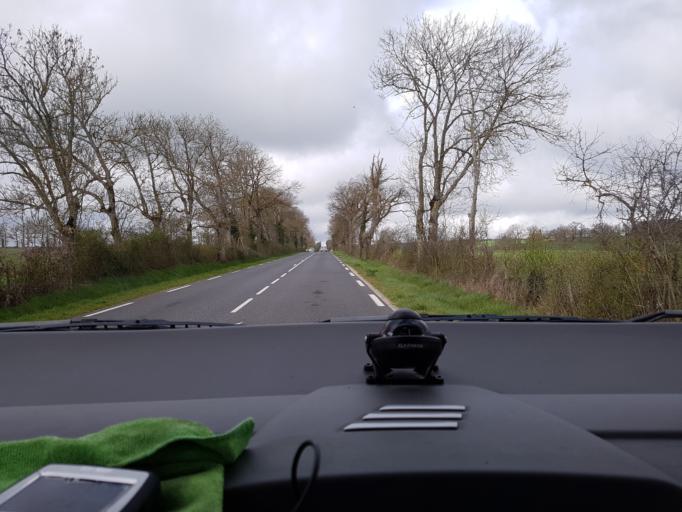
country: FR
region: Midi-Pyrenees
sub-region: Departement de l'Aveyron
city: Druelle
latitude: 44.3697
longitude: 2.4874
